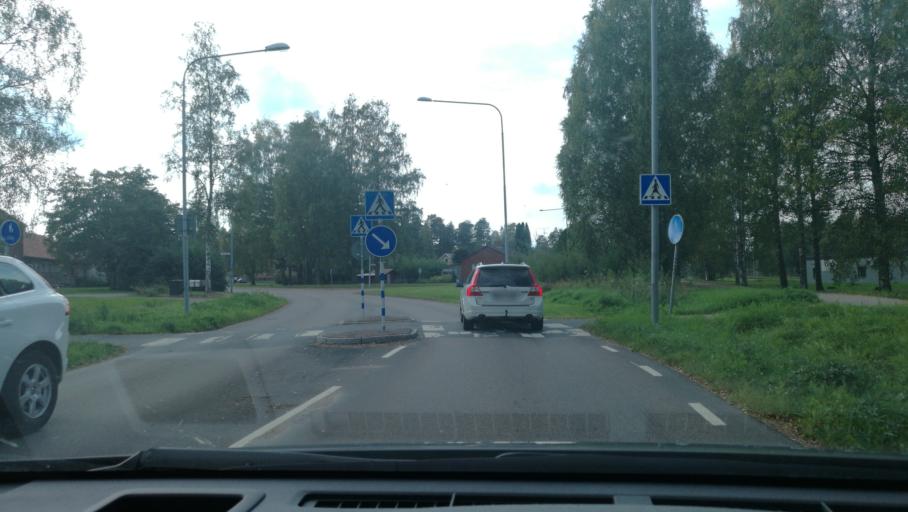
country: SE
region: Dalarna
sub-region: Avesta Kommun
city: Avesta
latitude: 60.1623
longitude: 16.1898
